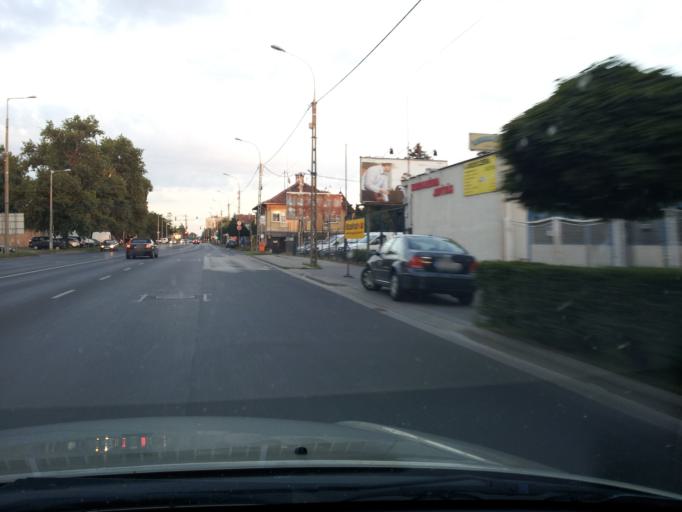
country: HU
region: Budapest
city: Budapest XV. keruelet
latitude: 47.5537
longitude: 19.1318
